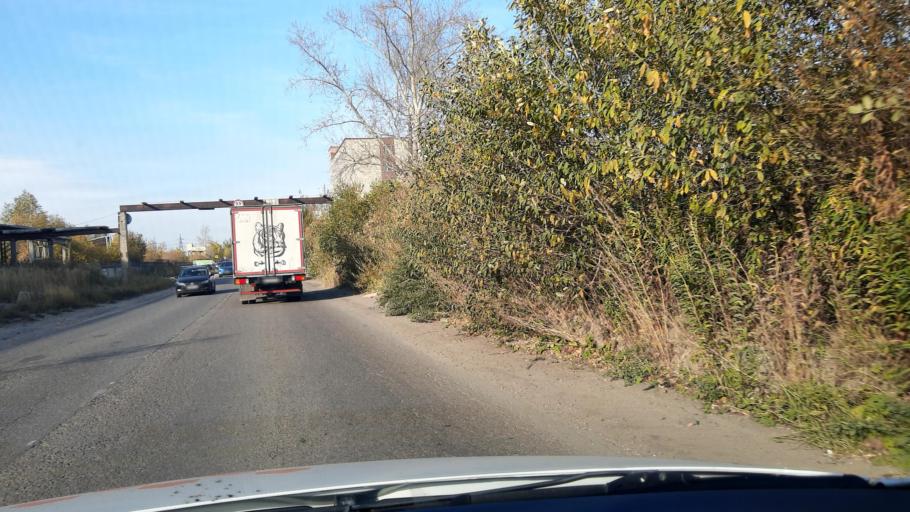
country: RU
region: Moskovskaya
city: Elektrostal'
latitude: 55.7714
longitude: 38.4714
